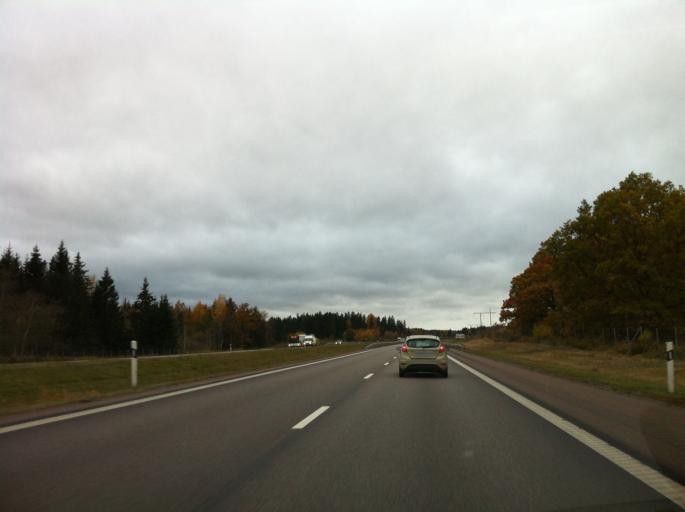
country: SE
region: OEstergoetland
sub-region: Boxholms Kommun
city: Boxholm
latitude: 58.3035
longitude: 14.9664
